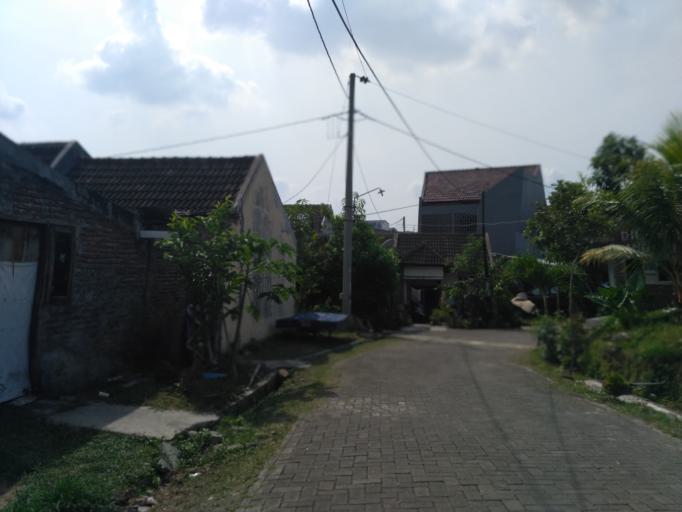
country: ID
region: Central Java
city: Semarang
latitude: -7.0389
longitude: 110.4370
